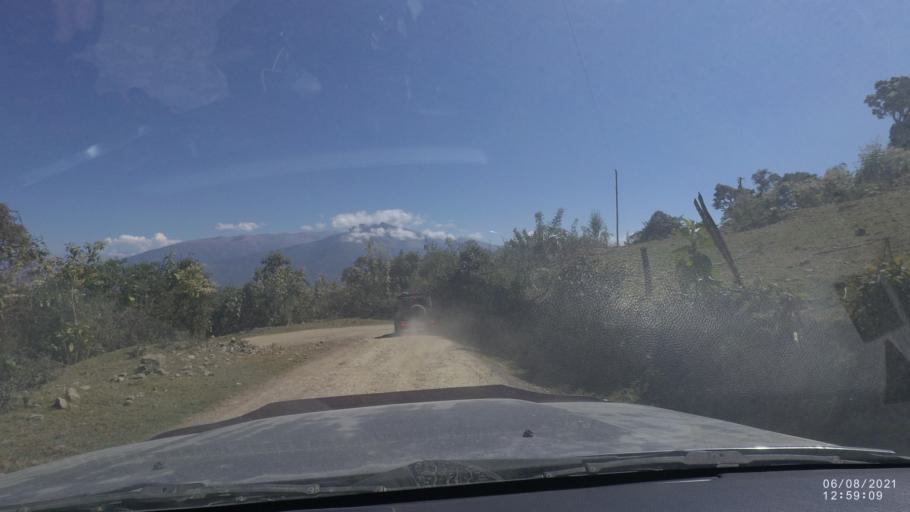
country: BO
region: Cochabamba
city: Colchani
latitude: -16.7498
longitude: -66.6865
